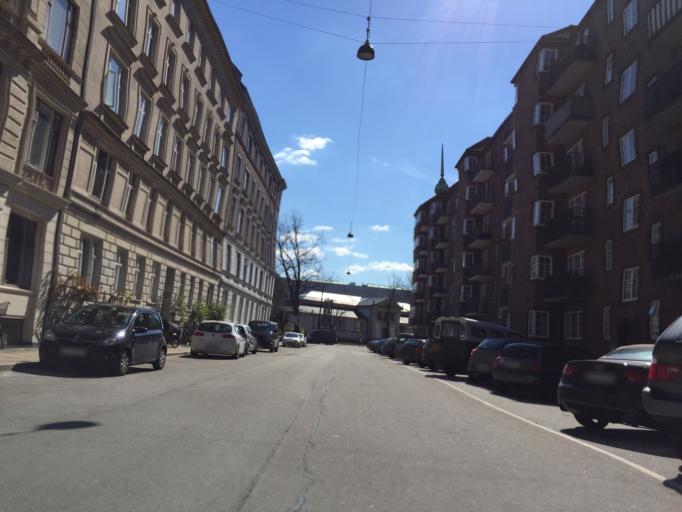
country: DK
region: Capital Region
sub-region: Kobenhavn
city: Copenhagen
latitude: 55.6912
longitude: 12.5775
